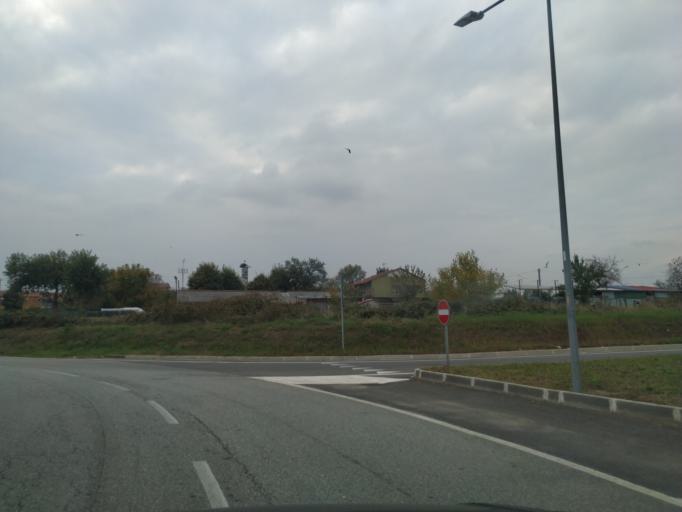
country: IT
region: Piedmont
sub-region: Provincia di Torino
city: Chivasso
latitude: 45.1959
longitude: 7.9168
